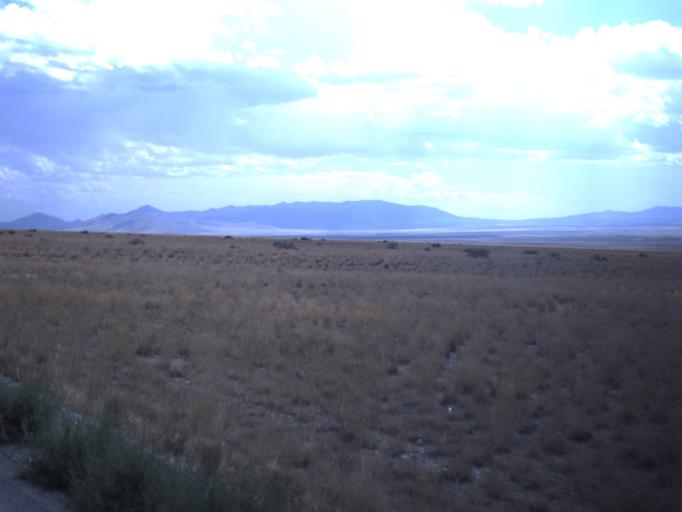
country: US
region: Utah
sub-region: Utah County
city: Eagle Mountain
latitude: 40.2684
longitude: -112.2416
